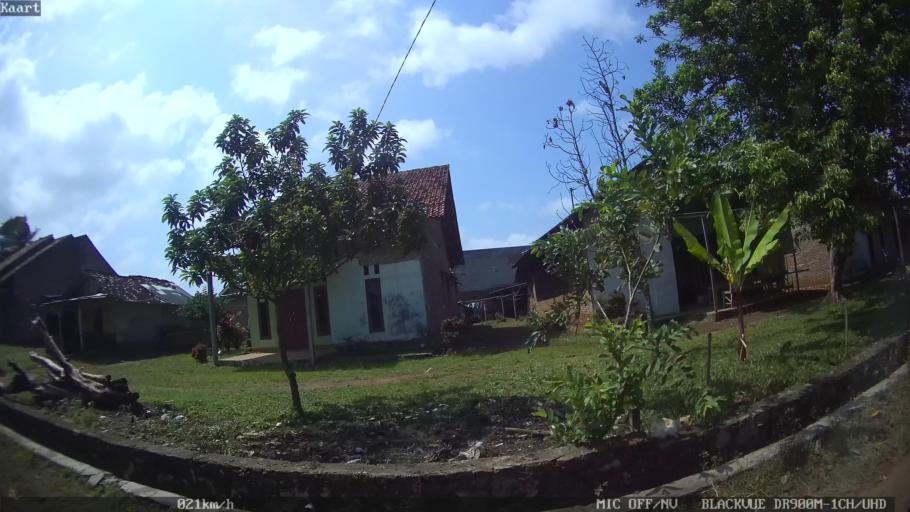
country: ID
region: Lampung
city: Kedaton
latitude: -5.3451
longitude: 105.2915
